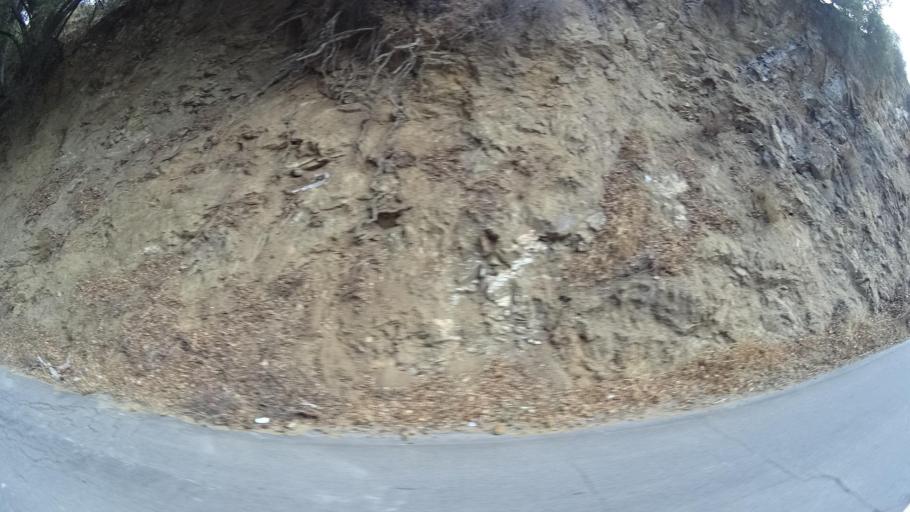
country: US
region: California
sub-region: San Diego County
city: Fallbrook
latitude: 33.4209
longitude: -117.2472
